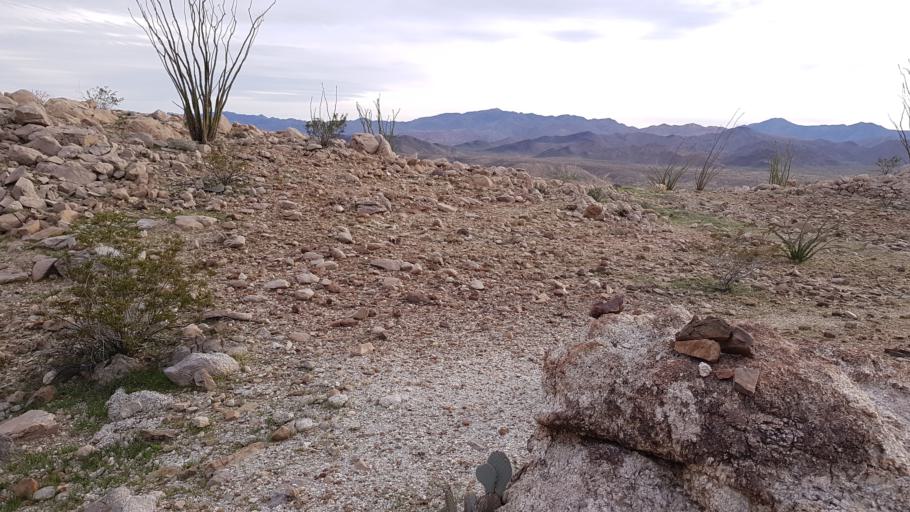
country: MX
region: Baja California
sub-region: Tecate
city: Cereso del Hongo
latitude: 32.8275
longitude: -116.1363
